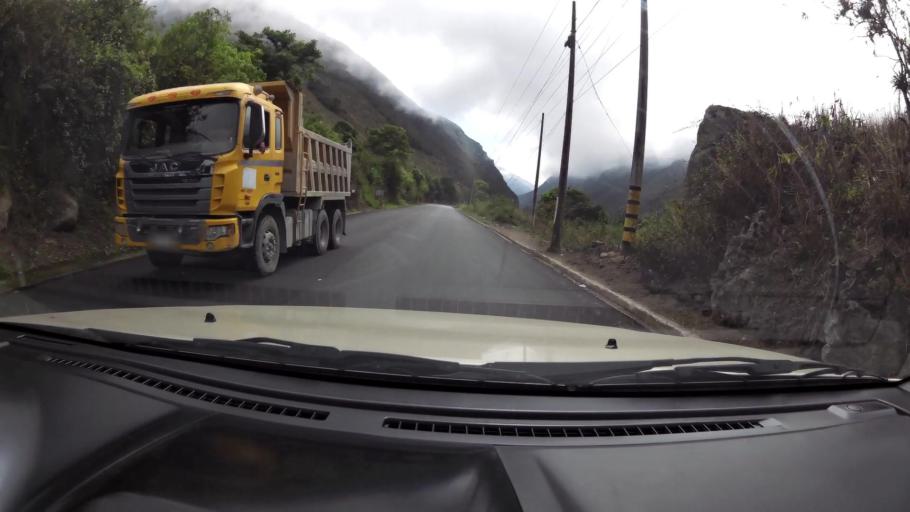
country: EC
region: El Oro
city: Pasaje
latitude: -3.3092
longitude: -79.5101
